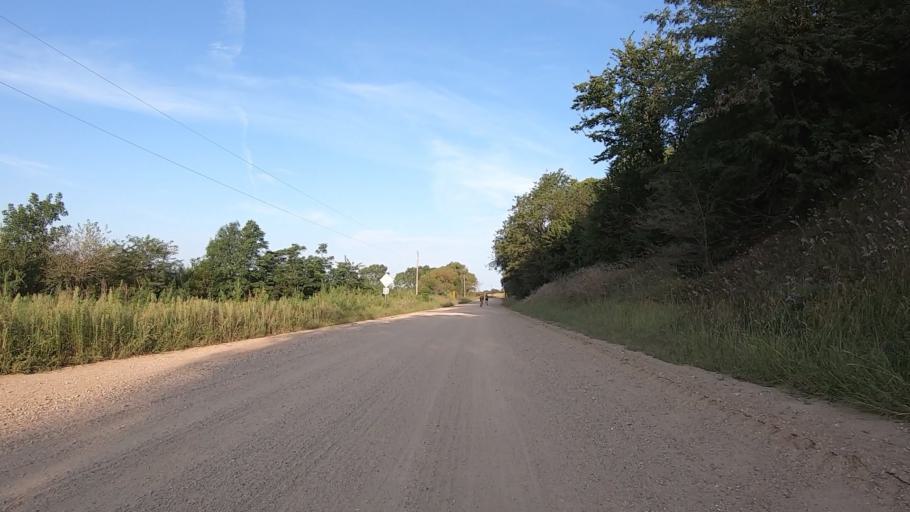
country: US
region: Kansas
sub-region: Marshall County
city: Blue Rapids
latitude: 39.7234
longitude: -96.7811
